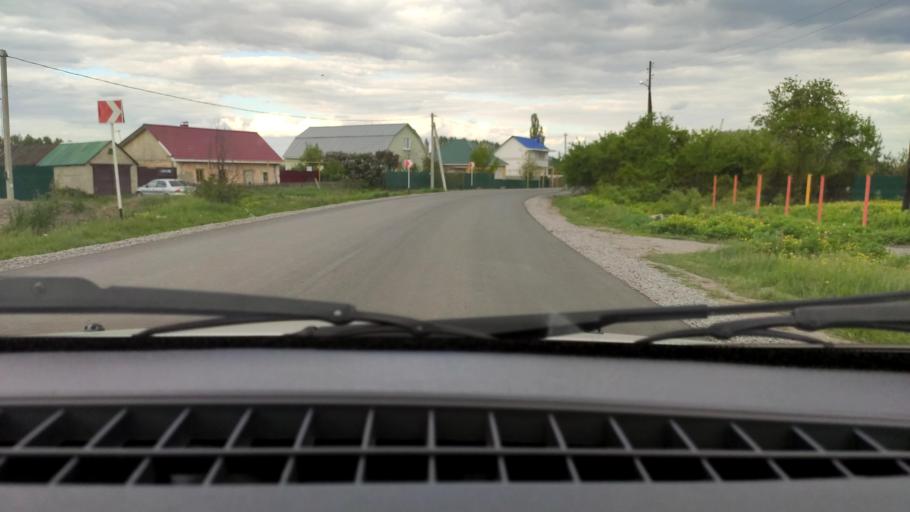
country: RU
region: Voronezj
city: Podkletnoye
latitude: 51.5891
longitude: 39.4645
